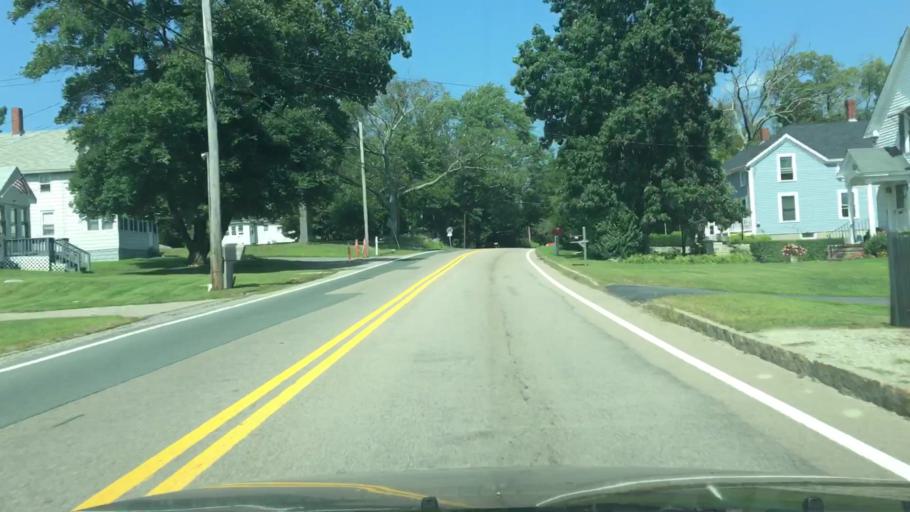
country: US
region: Massachusetts
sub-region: Worcester County
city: Milford
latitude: 42.1594
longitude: -71.4850
